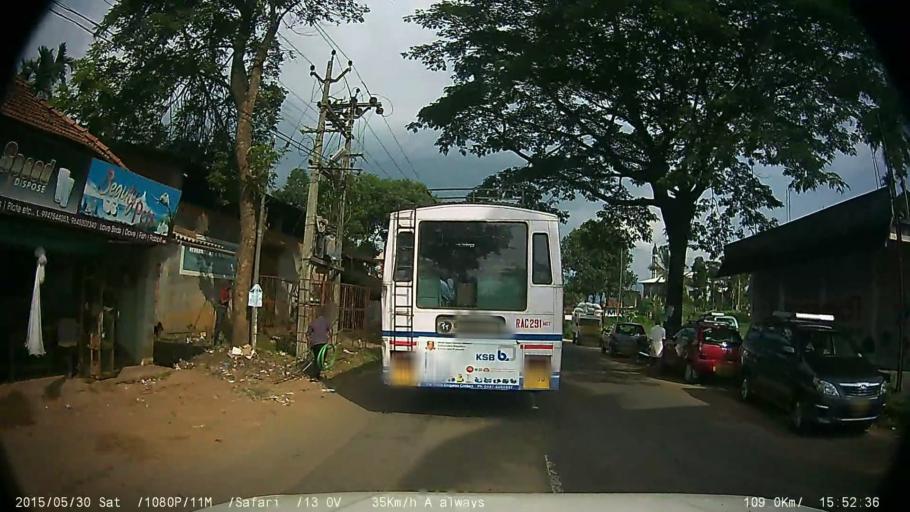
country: IN
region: Kerala
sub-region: Wayanad
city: Panamaram
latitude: 11.6769
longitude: 76.0750
